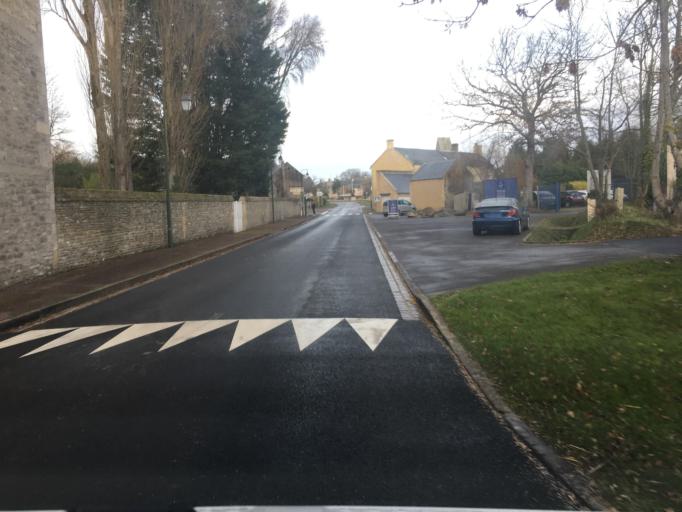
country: FR
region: Lower Normandy
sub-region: Departement du Calvados
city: Ver-sur-Mer
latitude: 49.3140
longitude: -0.5491
